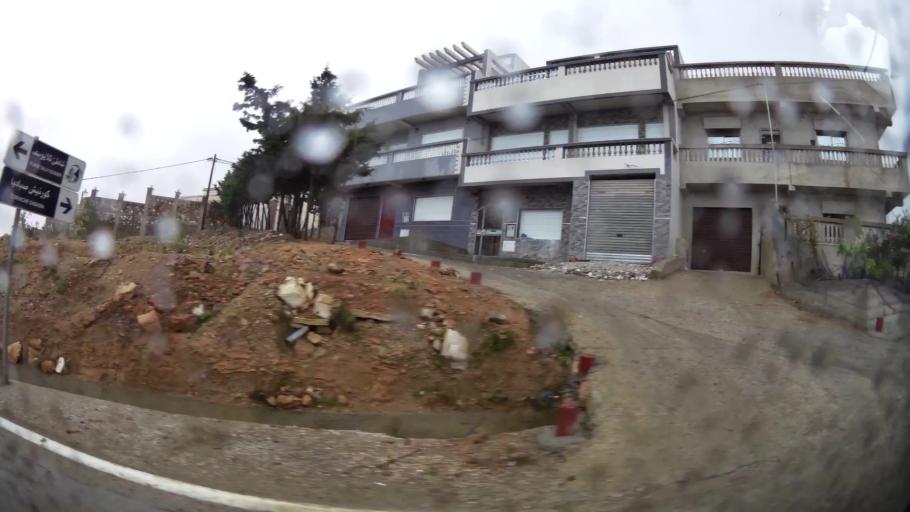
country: MA
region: Taza-Al Hoceima-Taounate
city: Tirhanimine
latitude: 35.2405
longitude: -3.9675
